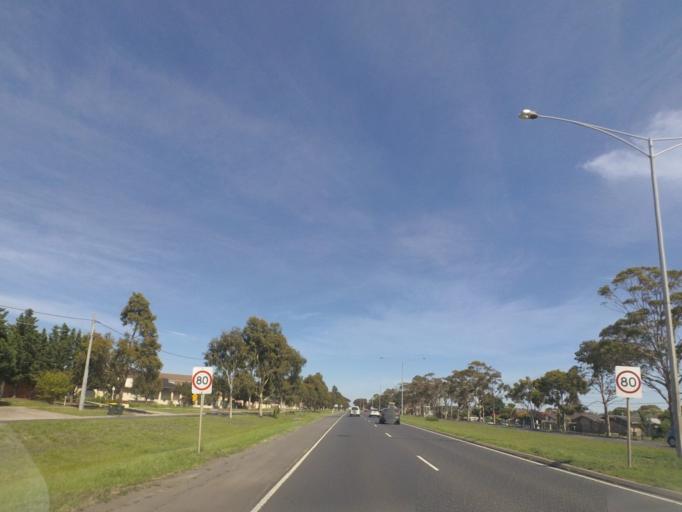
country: AU
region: Victoria
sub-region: Brimbank
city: Deer Park
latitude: -37.7675
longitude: 144.7658
